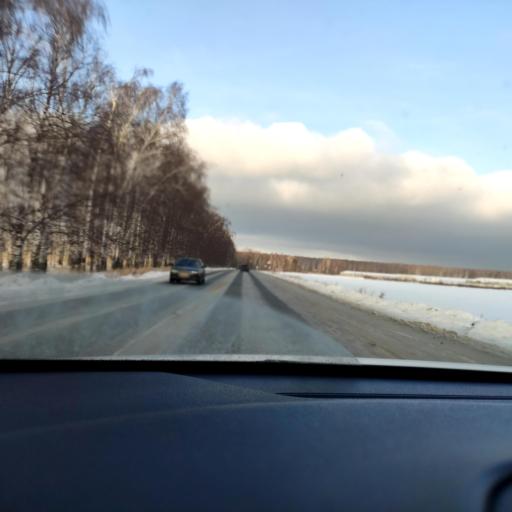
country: RU
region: Tatarstan
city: Osinovo
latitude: 55.8915
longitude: 48.8902
